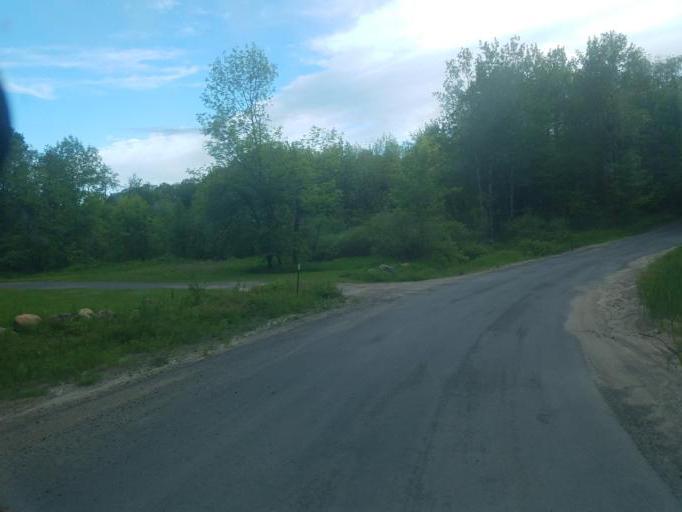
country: US
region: New York
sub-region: Herkimer County
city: Herkimer
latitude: 43.2275
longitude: -74.9682
